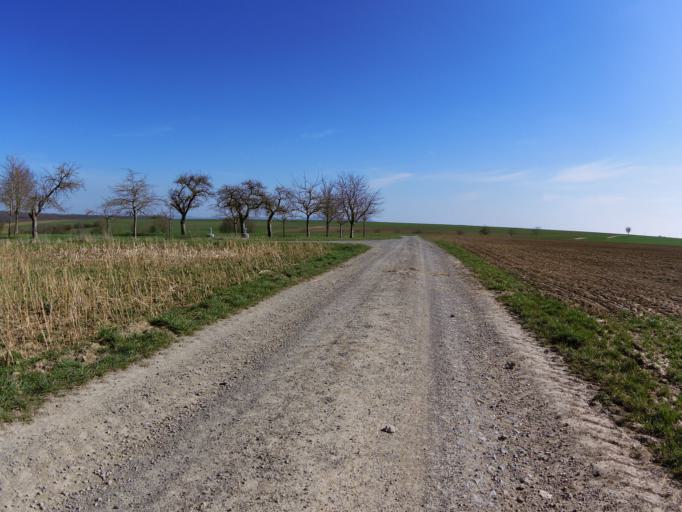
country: DE
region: Bavaria
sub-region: Regierungsbezirk Unterfranken
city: Prosselsheim
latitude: 49.8560
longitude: 10.1204
